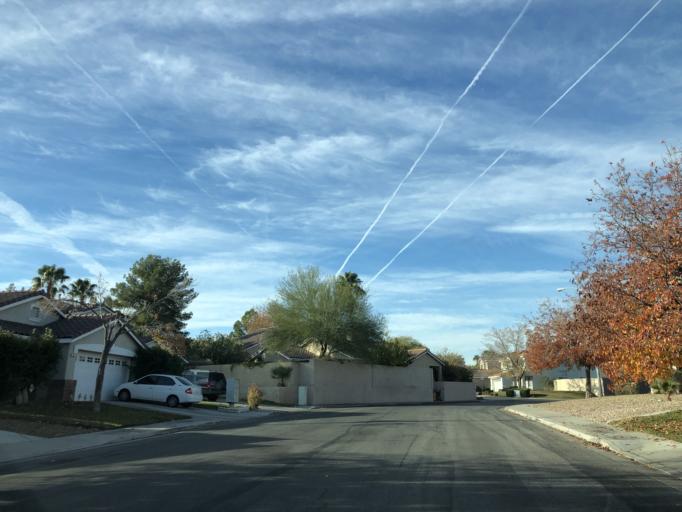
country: US
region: Nevada
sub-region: Clark County
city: Whitney
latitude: 36.0237
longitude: -115.0703
